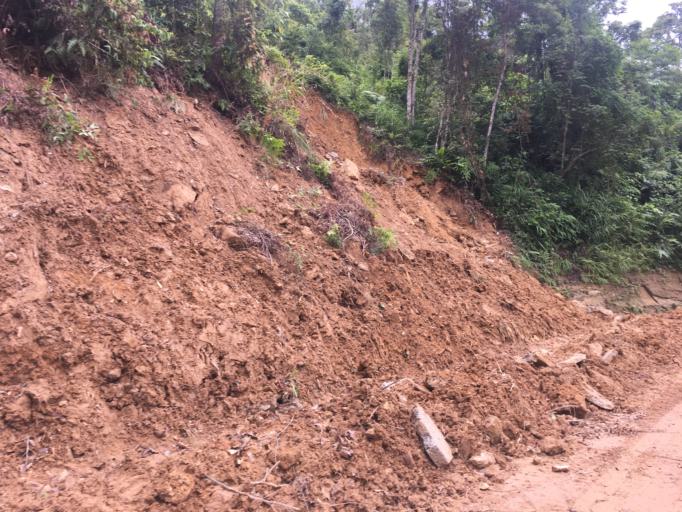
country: VN
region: Ha Giang
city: Thi Tran Tam Son
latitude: 22.9923
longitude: 105.0682
